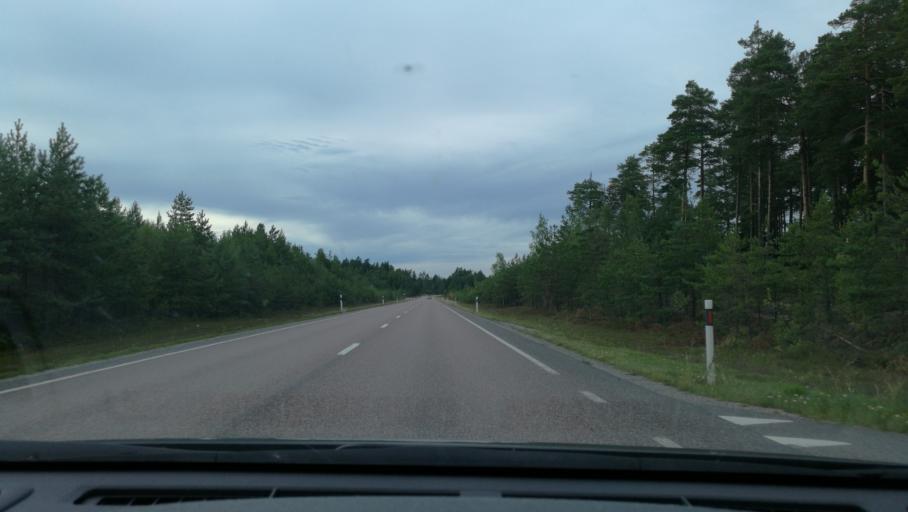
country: SE
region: Vaestmanland
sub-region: Kungsors Kommun
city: Kungsoer
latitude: 59.3718
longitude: 16.1105
